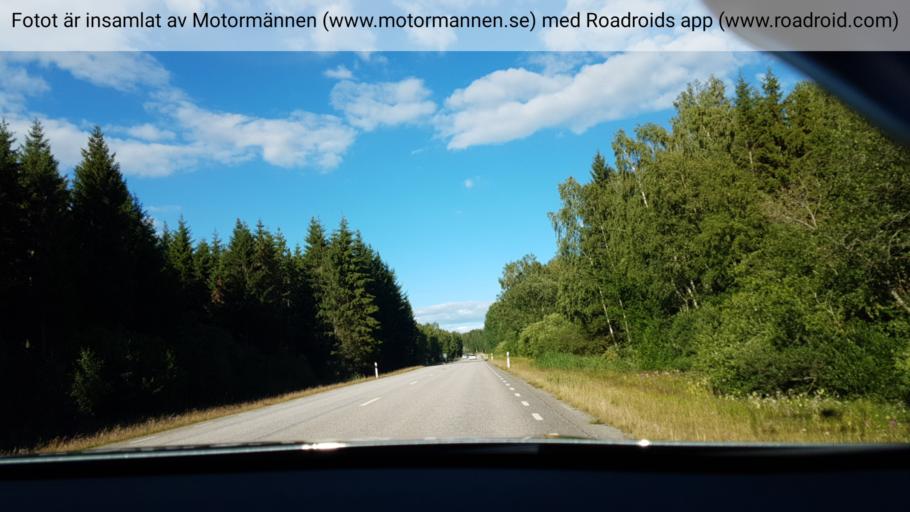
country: SE
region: Vaestra Goetaland
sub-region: Karlsborgs Kommun
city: Molltorp
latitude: 58.4751
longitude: 14.3320
